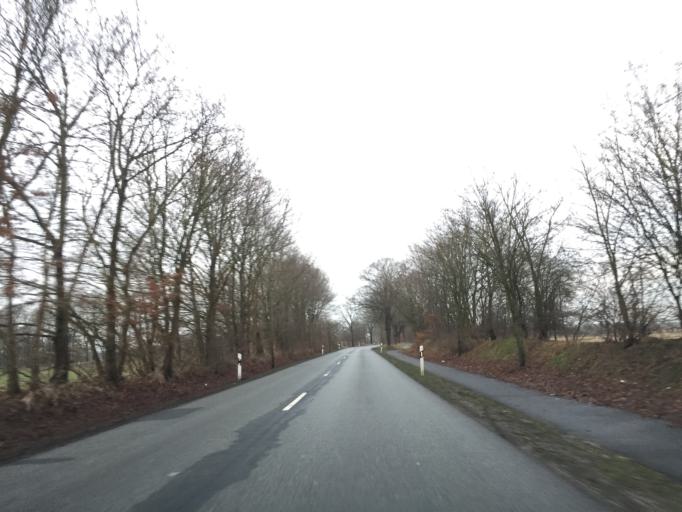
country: DE
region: Schleswig-Holstein
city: Wahlstedt
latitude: 53.9598
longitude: 10.1949
